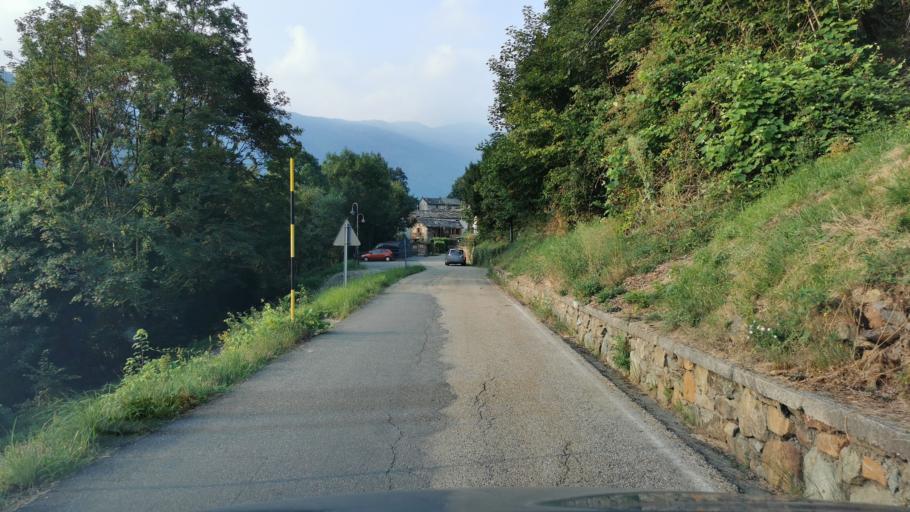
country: IT
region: Piedmont
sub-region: Provincia di Torino
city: La Villa
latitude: 45.2595
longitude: 7.4331
